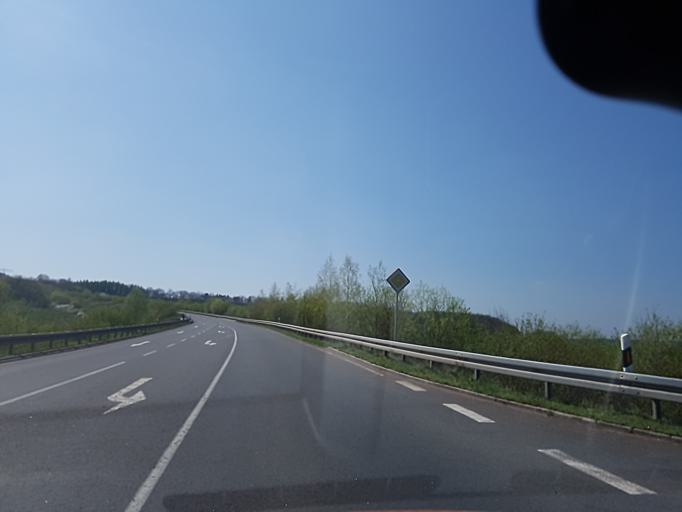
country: DE
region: Saxony
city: Leisnig
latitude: 51.1727
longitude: 12.9089
